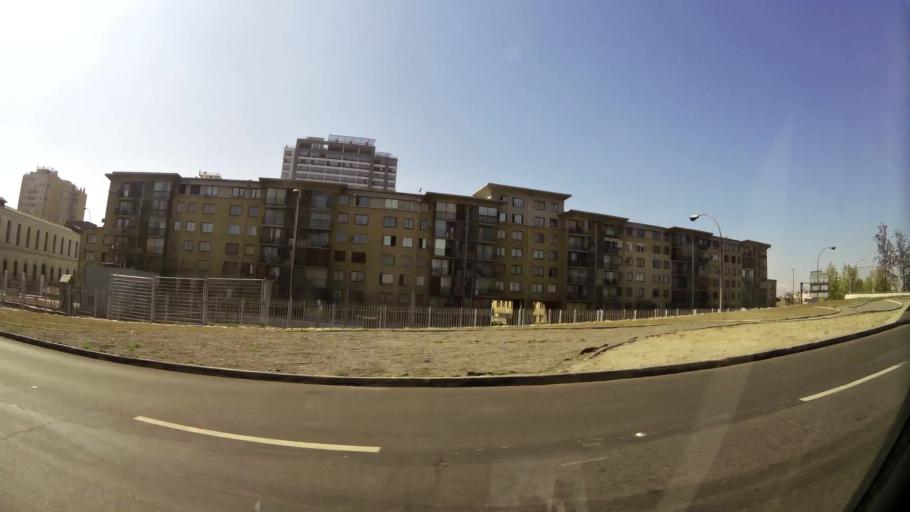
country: CL
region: Santiago Metropolitan
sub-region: Provincia de Santiago
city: Santiago
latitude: -33.4585
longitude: -70.6570
